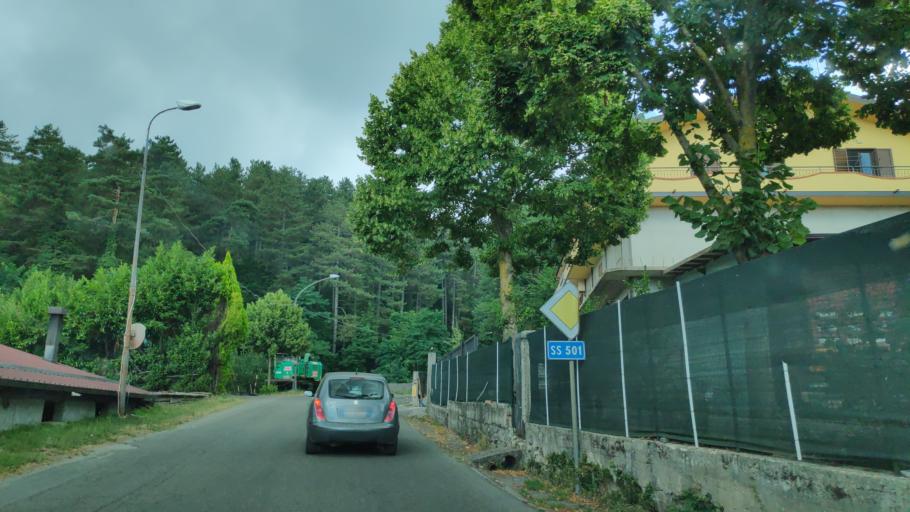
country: IT
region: Calabria
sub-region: Provincia di Vibo-Valentia
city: Mongiana
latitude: 38.5173
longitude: 16.3208
